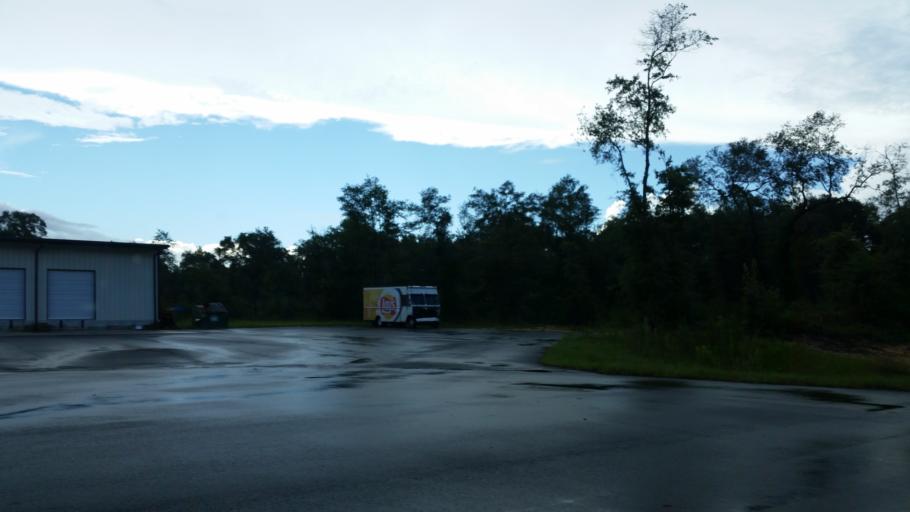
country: US
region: Florida
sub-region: Walton County
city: DeFuniak Springs
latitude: 30.7371
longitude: -86.3287
